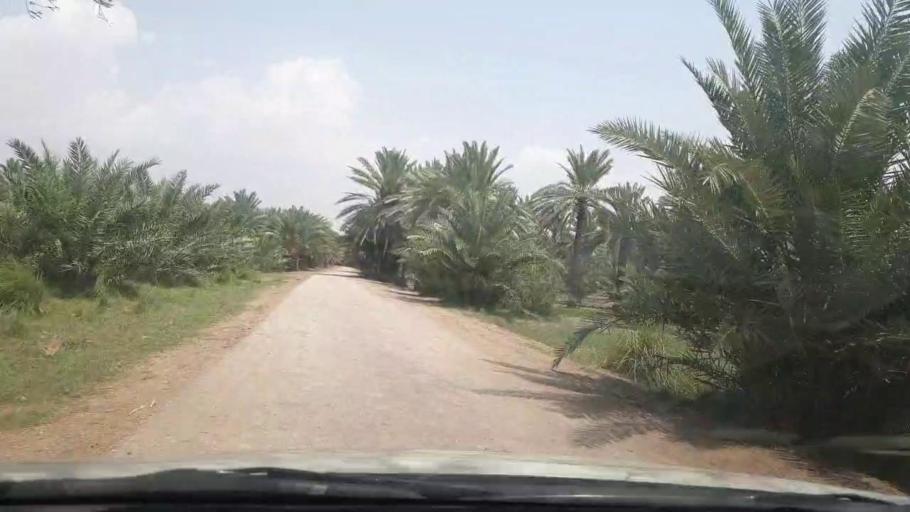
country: PK
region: Sindh
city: Khairpur
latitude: 27.5503
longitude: 68.8330
